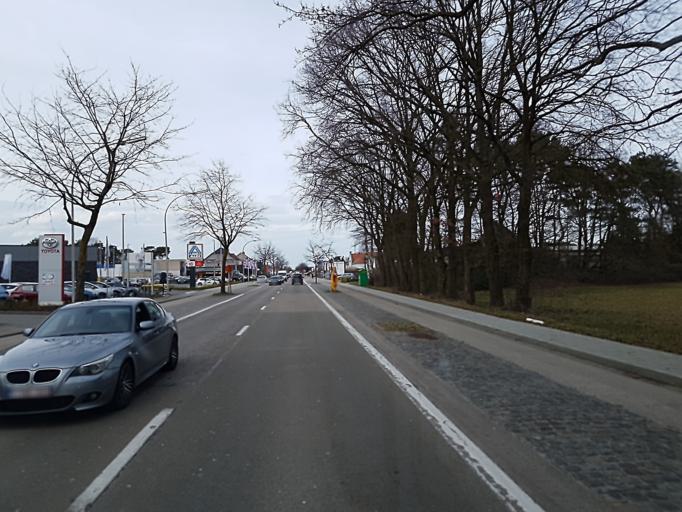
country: BE
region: Flanders
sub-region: Provincie Antwerpen
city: Mol
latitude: 51.2020
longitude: 5.1156
